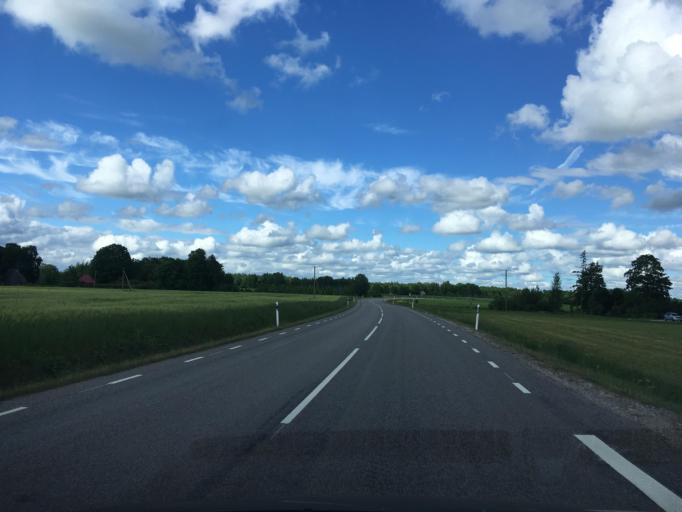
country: EE
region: Paernumaa
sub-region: Halinga vald
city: Parnu-Jaagupi
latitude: 58.6342
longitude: 24.5465
